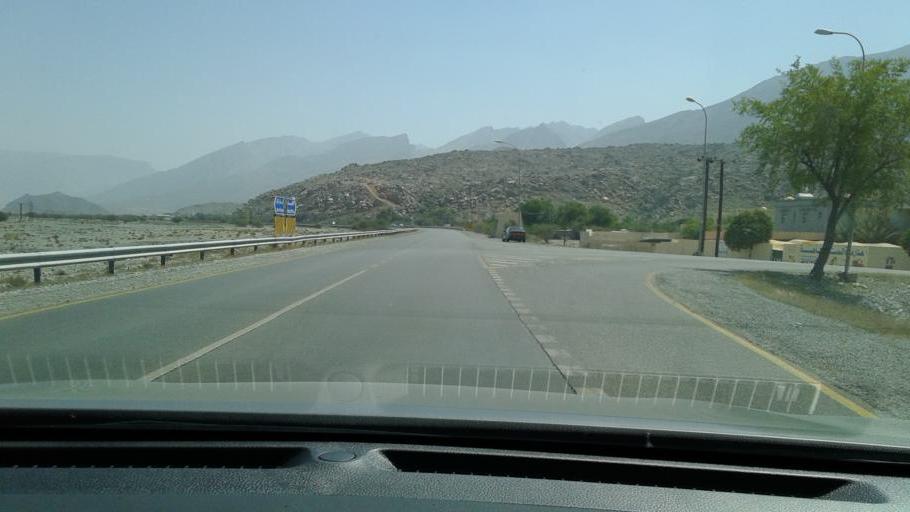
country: OM
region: Al Batinah
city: Rustaq
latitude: 23.3885
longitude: 57.4441
